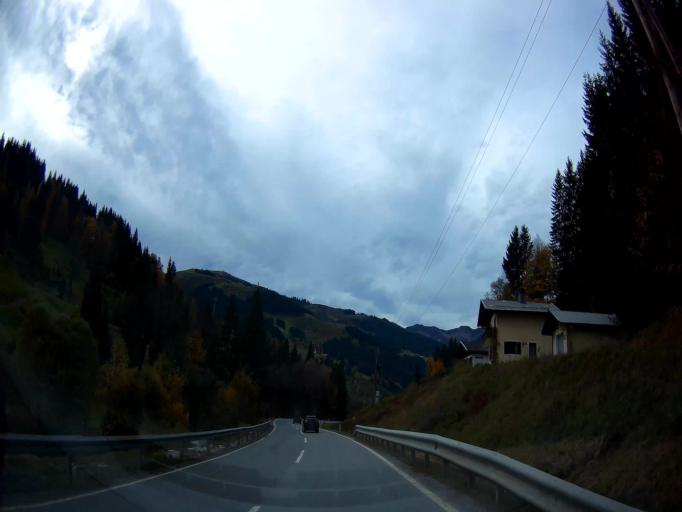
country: AT
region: Salzburg
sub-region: Politischer Bezirk Zell am See
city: Maria Alm am Steinernen Meer
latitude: 47.3914
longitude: 12.9469
